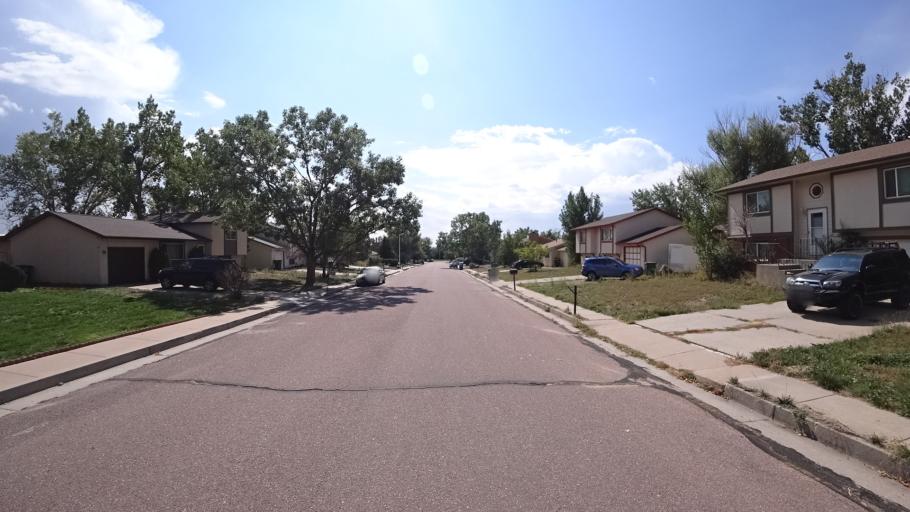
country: US
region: Colorado
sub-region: El Paso County
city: Cimarron Hills
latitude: 38.8624
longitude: -104.7241
